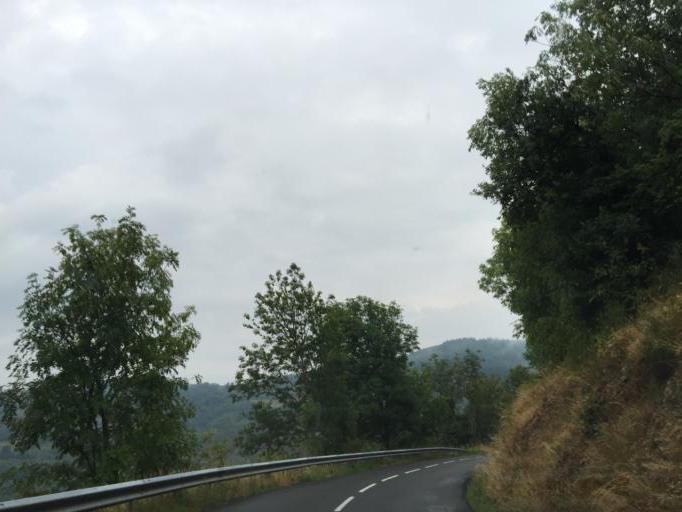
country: FR
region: Rhone-Alpes
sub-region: Departement de la Loire
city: Saint-Christo-en-Jarez
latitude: 45.5271
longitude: 4.4915
